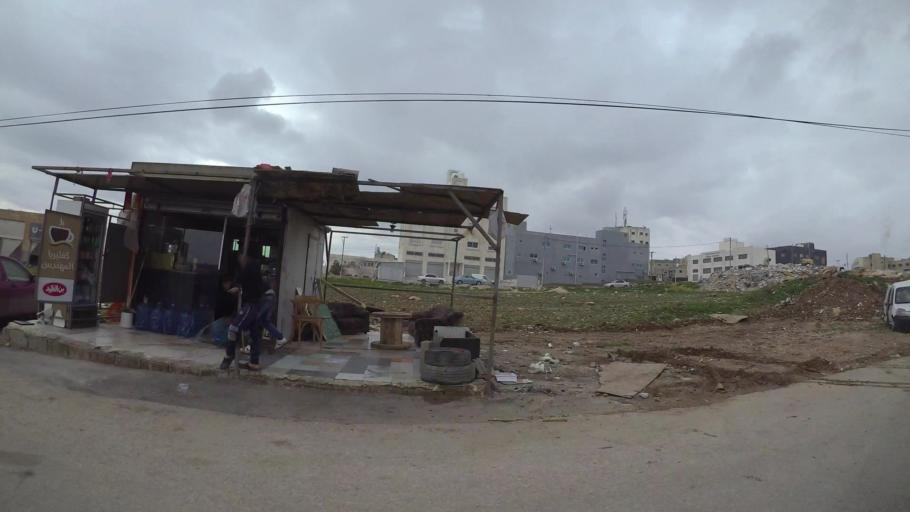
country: JO
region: Amman
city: Wadi as Sir
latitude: 31.9416
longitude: 35.8336
